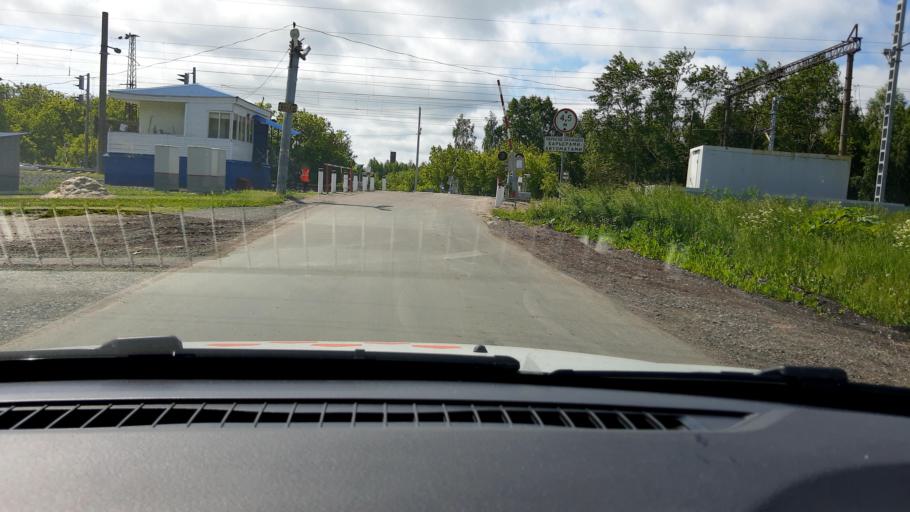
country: RU
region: Nizjnij Novgorod
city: Linda
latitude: 56.5507
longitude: 44.0638
